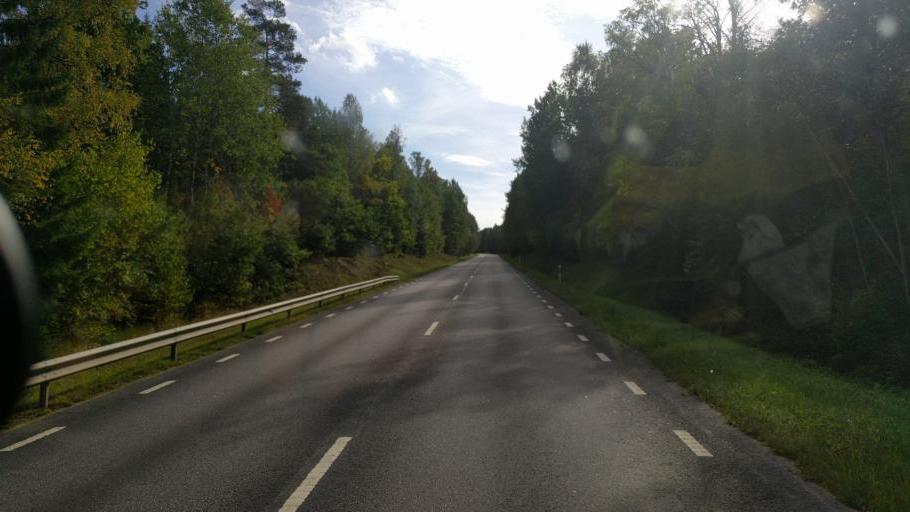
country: SE
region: OEstergoetland
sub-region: Kinda Kommun
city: Kisa
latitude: 57.9440
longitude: 15.6668
